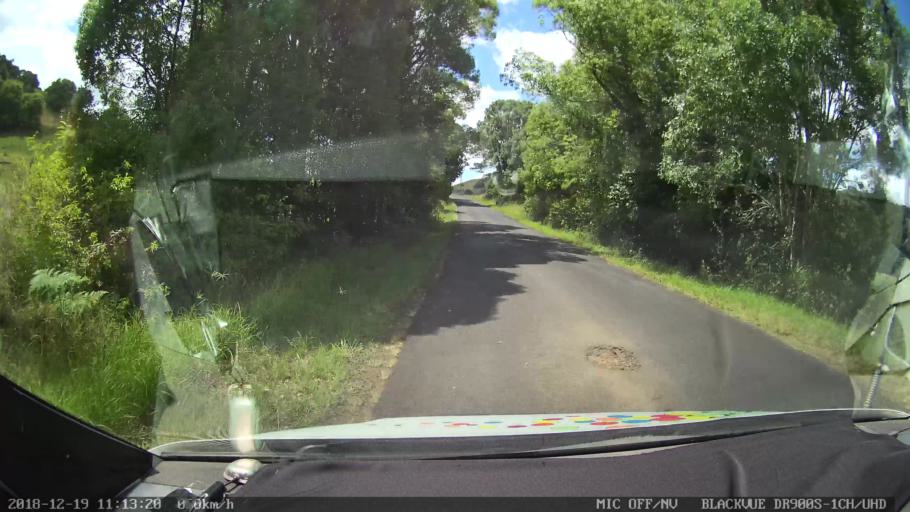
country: AU
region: New South Wales
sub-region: Lismore Municipality
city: Nimbin
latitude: -28.6551
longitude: 153.2634
